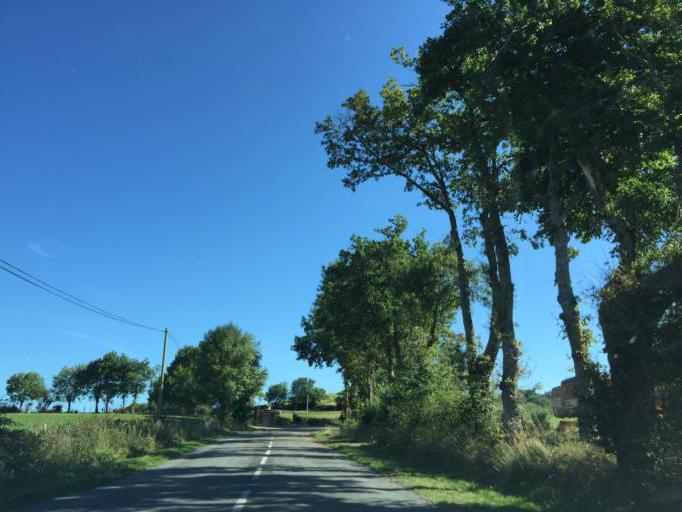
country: FR
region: Midi-Pyrenees
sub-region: Departement de l'Aveyron
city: Pont-de-Salars
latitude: 44.3306
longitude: 2.7644
